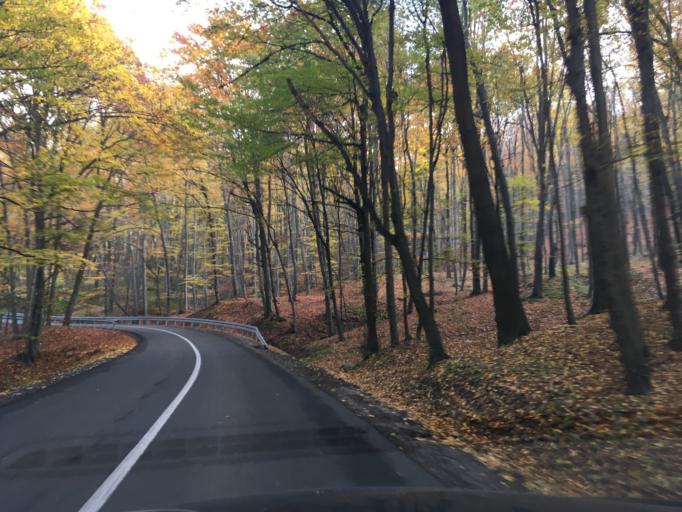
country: RS
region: Central Serbia
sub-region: Belgrade
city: Sopot
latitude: 44.4714
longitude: 20.5651
